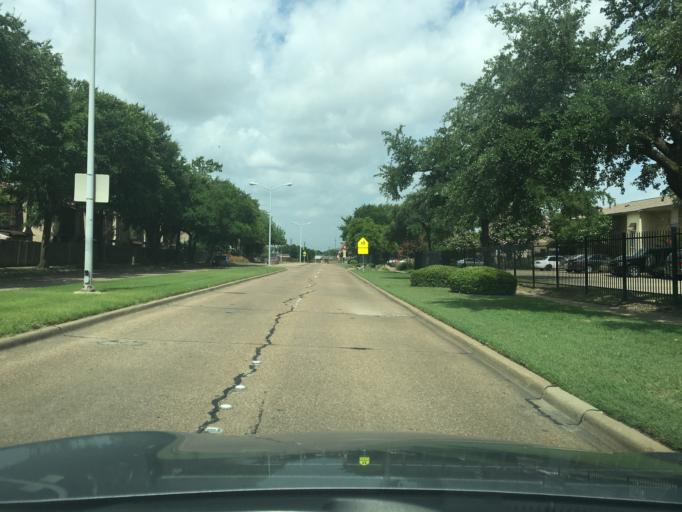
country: US
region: Texas
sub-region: Dallas County
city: Richardson
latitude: 32.9167
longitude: -96.7033
